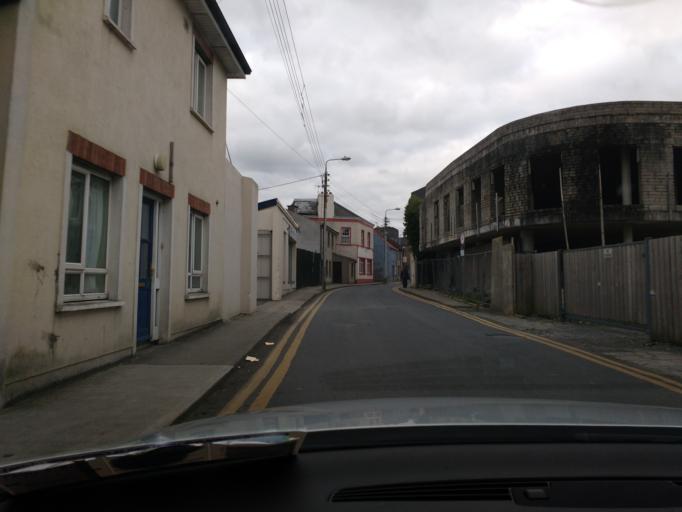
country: IE
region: Munster
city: Thurles
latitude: 52.6773
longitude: -7.8149
